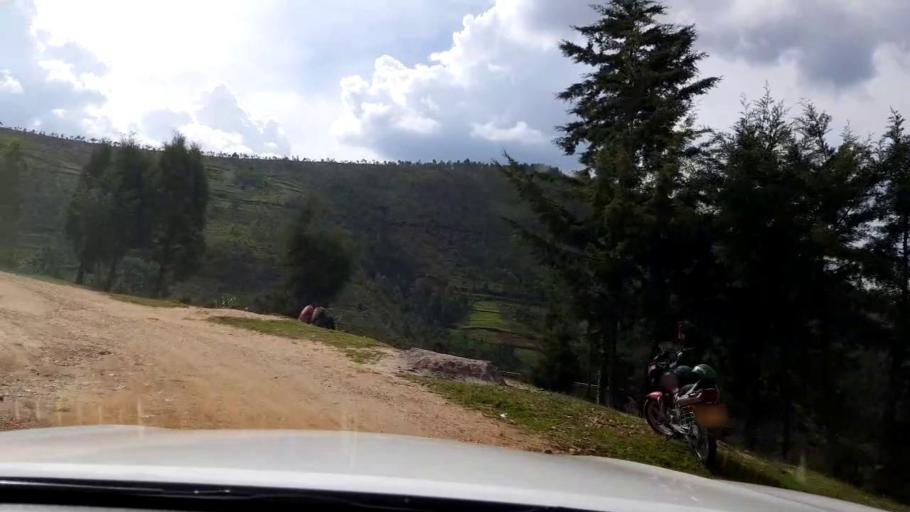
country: RW
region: Southern Province
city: Gitarama
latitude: -1.9944
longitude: 29.7120
